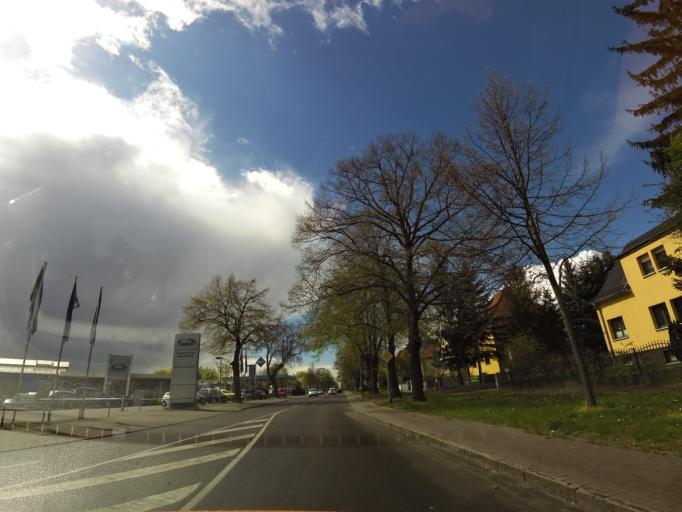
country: DE
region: Saxony-Anhalt
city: Diesdorf
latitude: 52.1059
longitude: 11.5908
